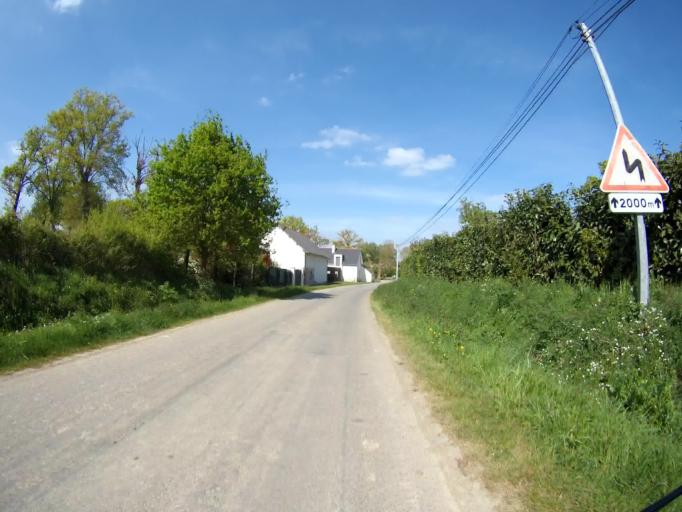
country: FR
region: Brittany
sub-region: Departement d'Ille-et-Vilaine
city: Saint-Erblon
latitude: 48.0251
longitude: -1.6287
